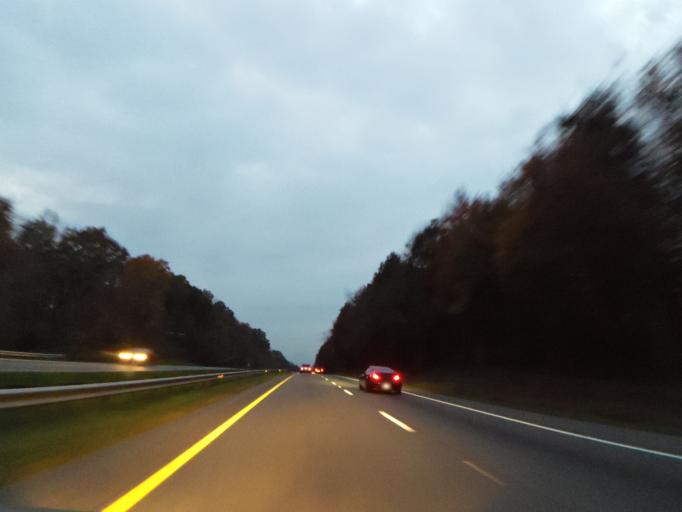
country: US
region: North Carolina
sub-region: McDowell County
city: West Marion
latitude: 35.6358
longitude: -82.0971
